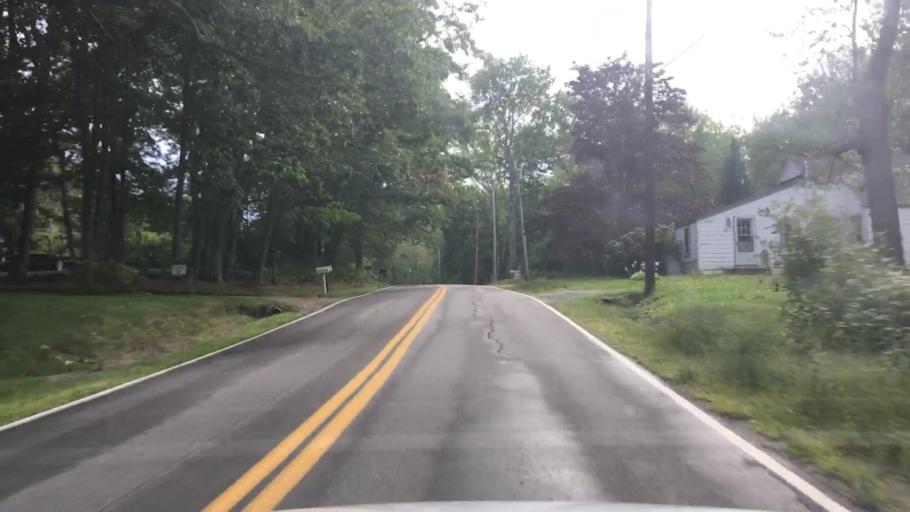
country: US
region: Maine
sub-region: Hancock County
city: Trenton
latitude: 44.4668
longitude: -68.4232
